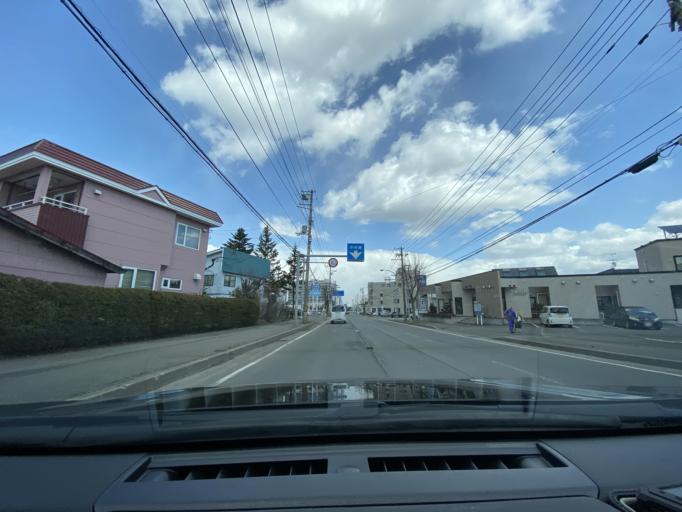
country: JP
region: Hokkaido
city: Kitahiroshima
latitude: 42.9730
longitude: 141.4779
